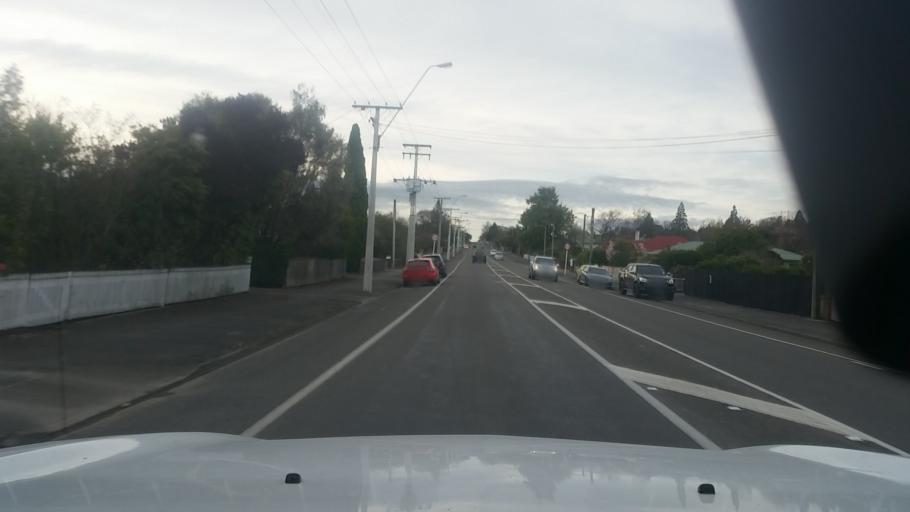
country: NZ
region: Wellington
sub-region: Masterton District
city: Masterton
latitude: -40.9418
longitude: 175.6699
